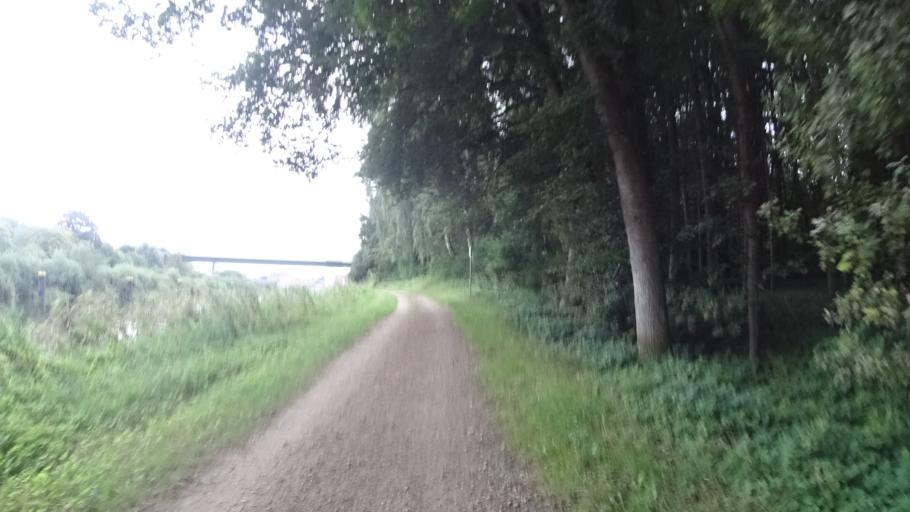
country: DE
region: Schleswig-Holstein
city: Alt Molln
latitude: 53.6313
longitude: 10.6680
